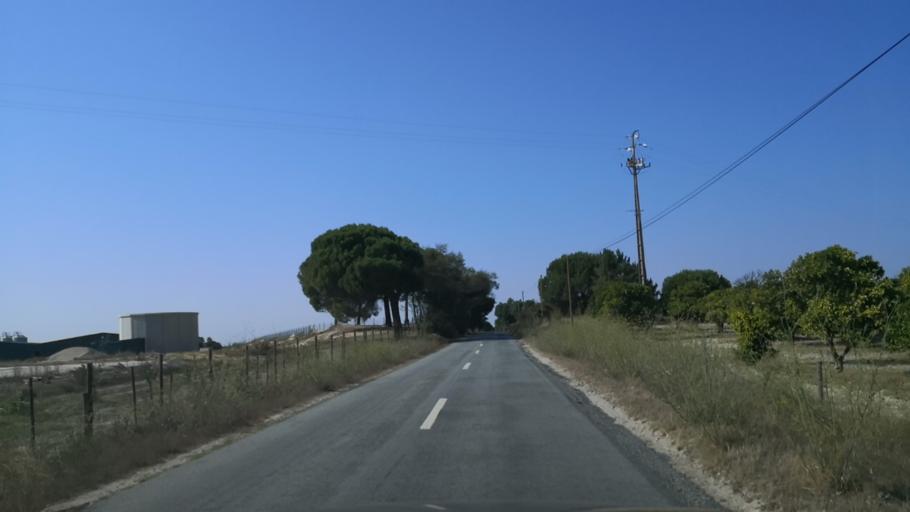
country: PT
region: Evora
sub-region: Vendas Novas
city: Vendas Novas
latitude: 38.7205
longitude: -8.6192
